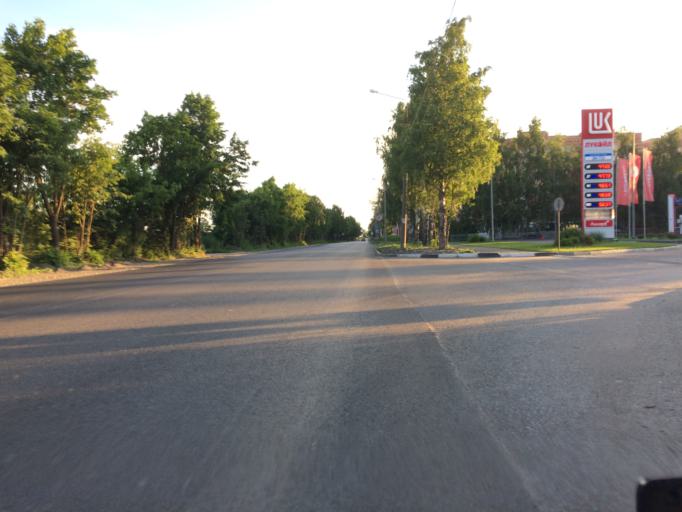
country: RU
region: Mariy-El
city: Medvedevo
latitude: 56.6428
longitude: 47.8316
